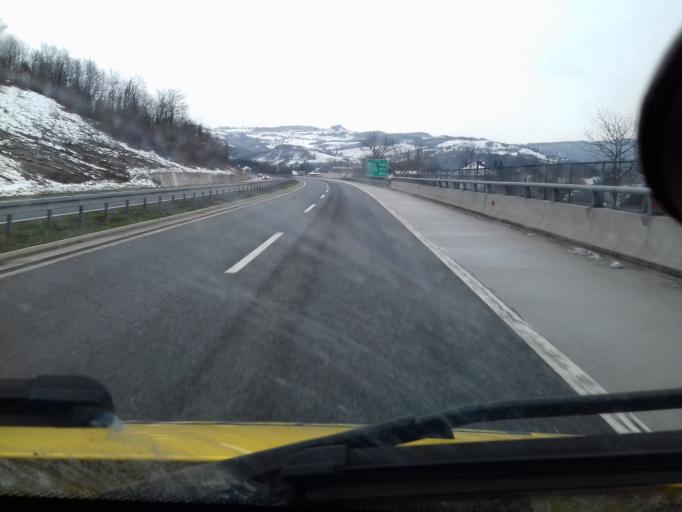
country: BA
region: Federation of Bosnia and Herzegovina
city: Visoko
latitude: 44.0005
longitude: 18.1805
